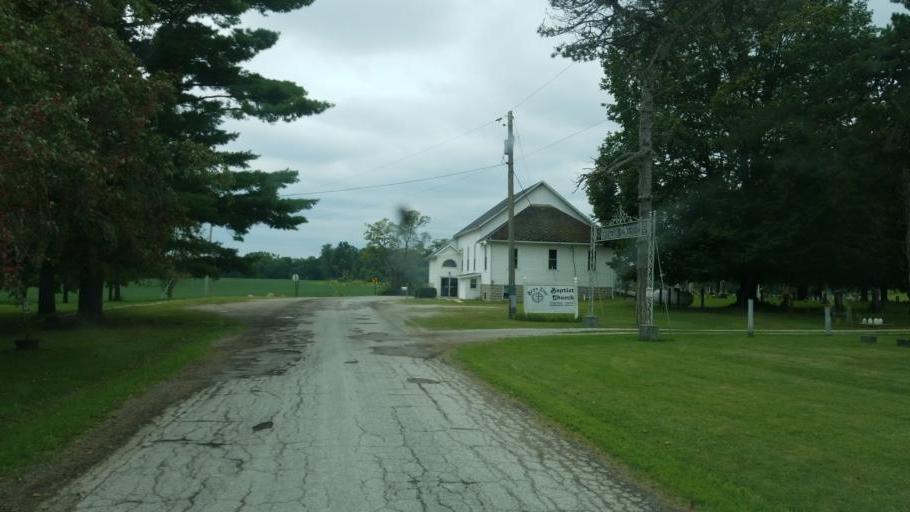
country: US
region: Ohio
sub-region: Morrow County
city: Mount Gilead
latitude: 40.5568
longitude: -82.7671
